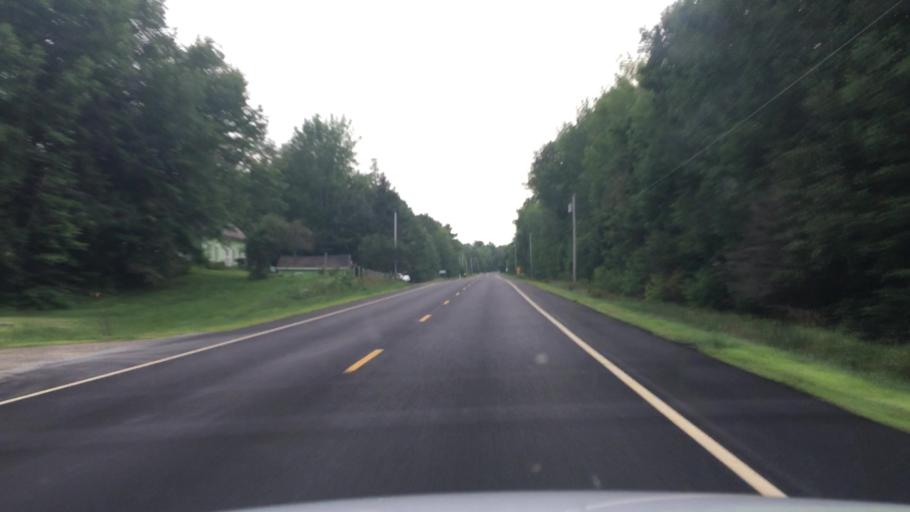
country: US
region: Maine
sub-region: Waldo County
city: Searsmont
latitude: 44.4025
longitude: -69.2369
